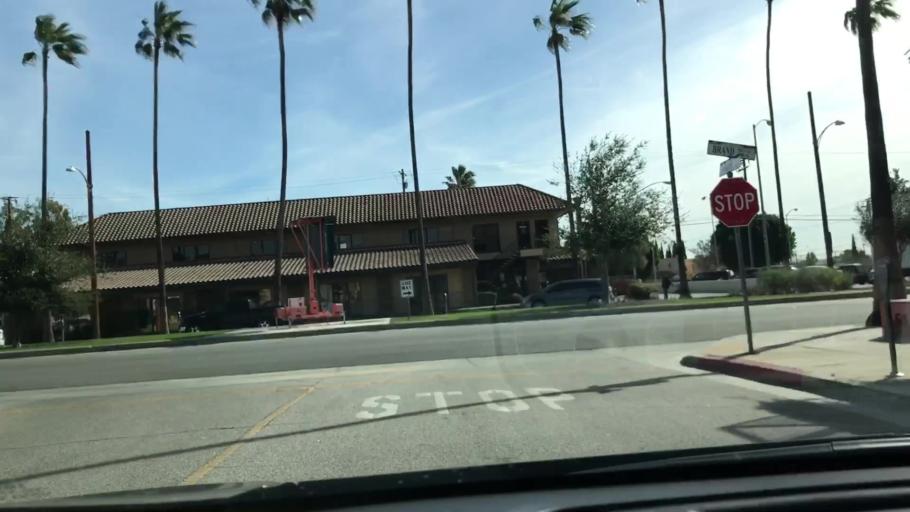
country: US
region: California
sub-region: Los Angeles County
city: San Fernando
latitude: 34.2802
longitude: -118.4423
